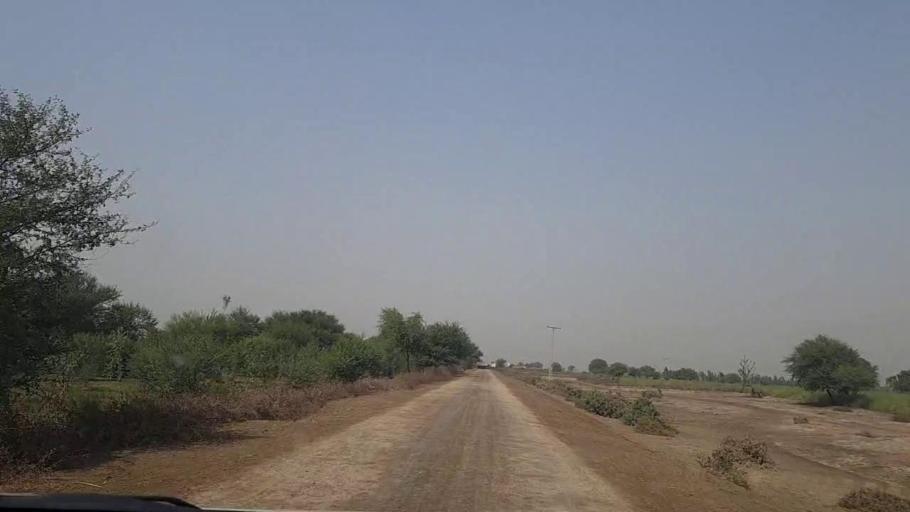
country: PK
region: Sindh
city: Mirpur Khas
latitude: 25.6240
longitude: 69.1995
